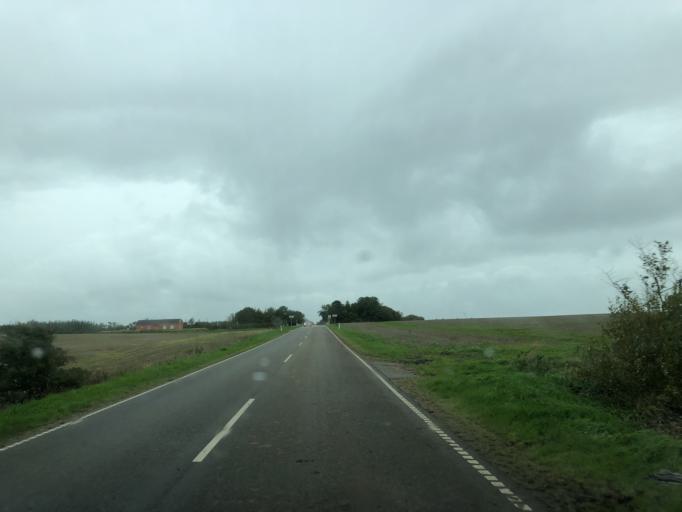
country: DK
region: North Denmark
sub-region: Thisted Kommune
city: Hurup
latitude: 56.7202
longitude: 8.3710
